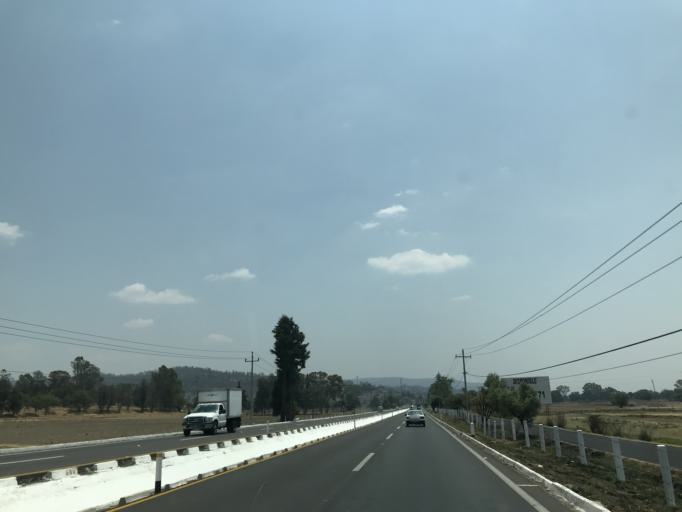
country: MX
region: Tlaxcala
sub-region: Ixtacuixtla de Mariano Matamoros
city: Villa Mariano Matamoros
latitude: 19.3275
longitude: -98.3635
